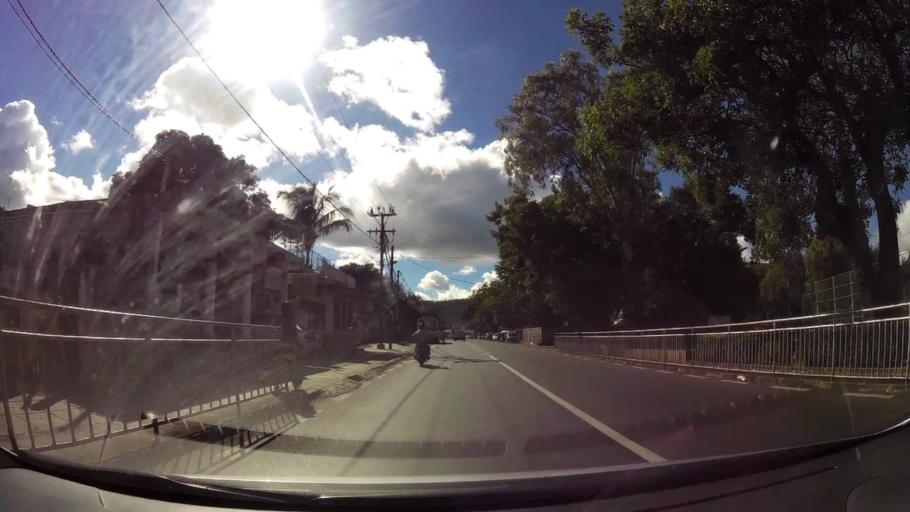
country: MU
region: Pamplemousses
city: Le Hochet
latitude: -20.1474
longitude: 57.5215
